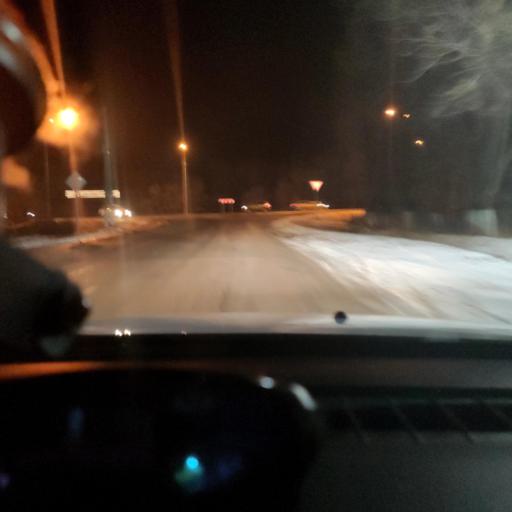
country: RU
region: Samara
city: Samara
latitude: 53.0815
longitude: 50.0920
